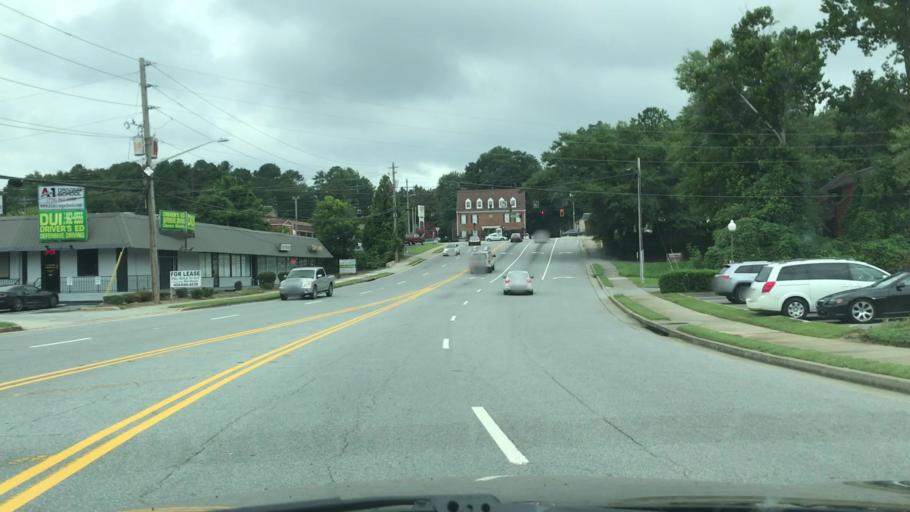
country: US
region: Georgia
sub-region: Gwinnett County
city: Lawrenceville
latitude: 33.9561
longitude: -83.9980
